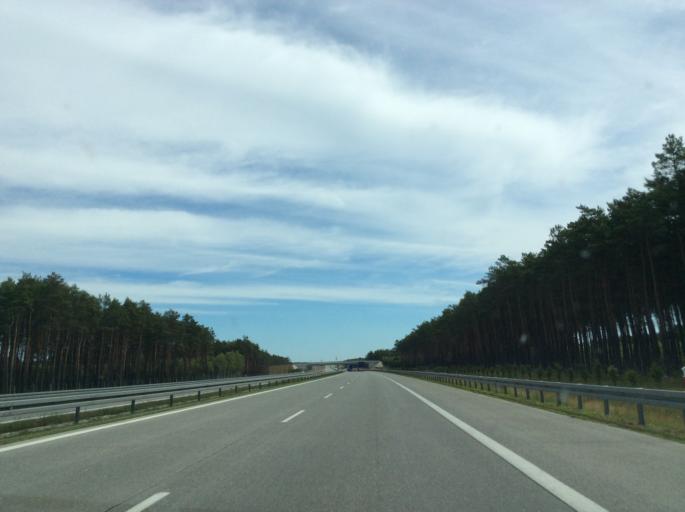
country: PL
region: Lubusz
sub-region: Powiat swiebodzinski
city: Szczaniec
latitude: 52.3006
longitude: 15.7411
